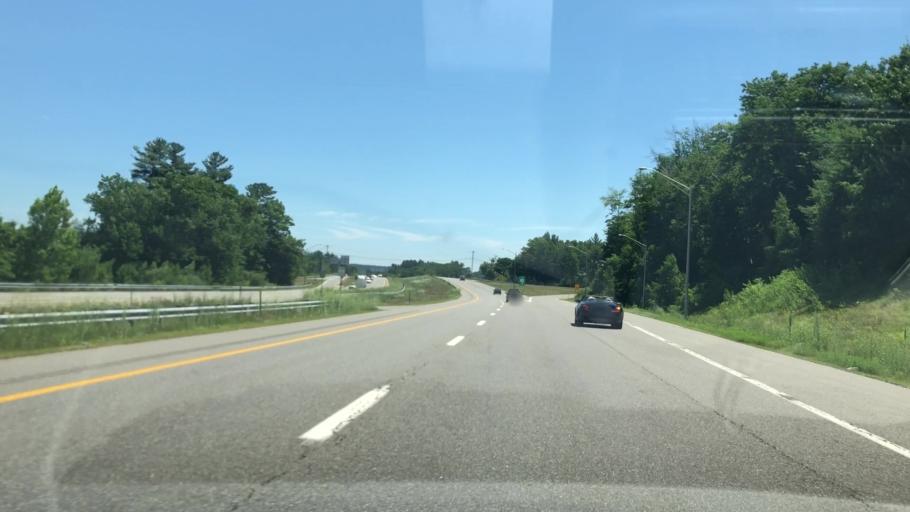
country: US
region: New Hampshire
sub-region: Hillsborough County
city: Bedford
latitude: 42.9534
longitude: -71.4827
